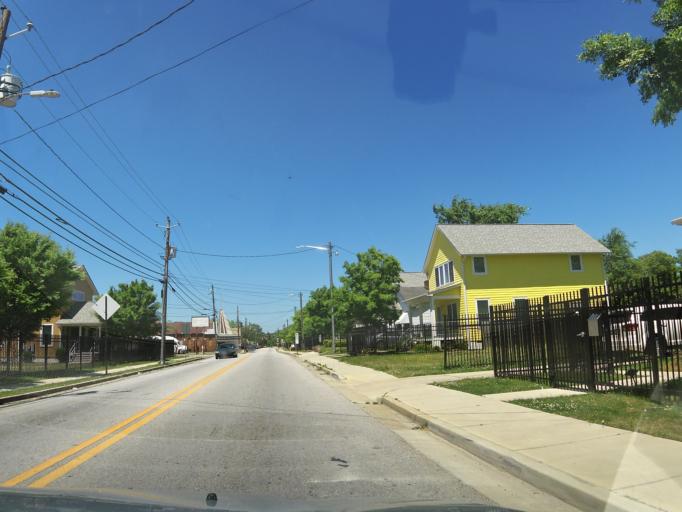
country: US
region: Georgia
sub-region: Richmond County
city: Augusta
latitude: 33.4615
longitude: -81.9814
